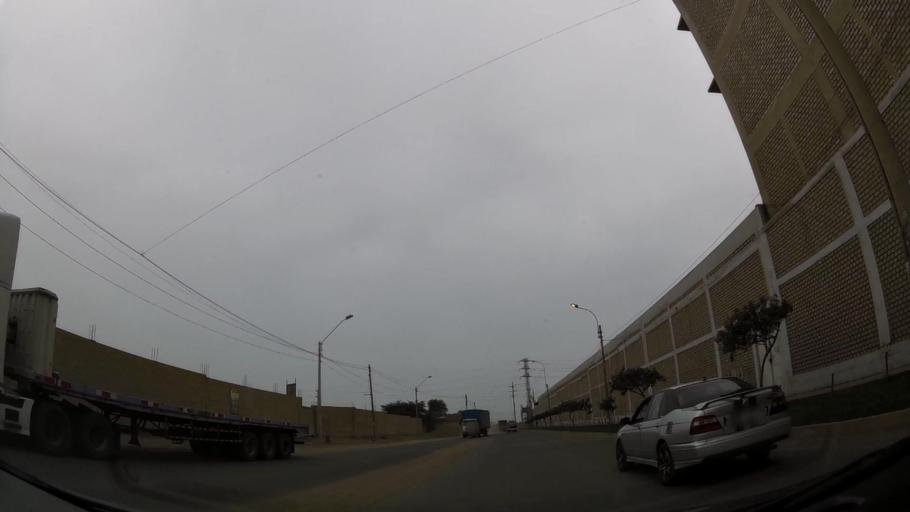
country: PE
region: Lima
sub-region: Lima
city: Punta Hermosa
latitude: -12.2992
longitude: -76.8423
